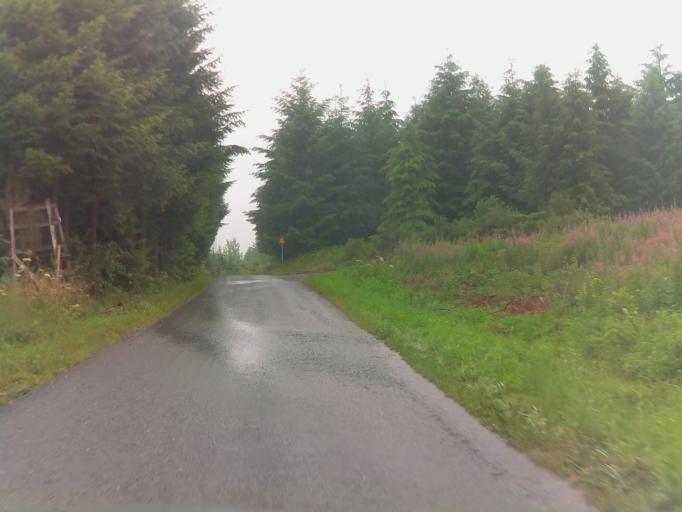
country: BE
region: Wallonia
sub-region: Province de Namur
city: Bievre
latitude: 49.9536
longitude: 5.0335
